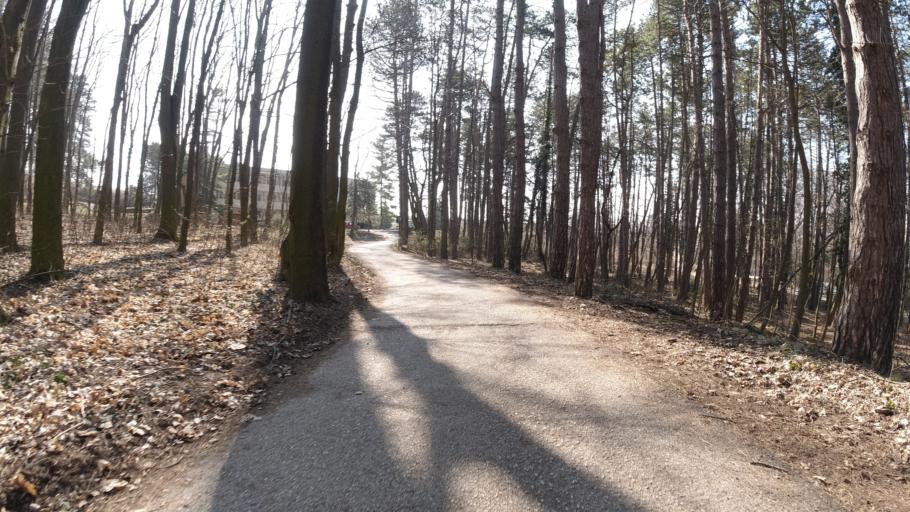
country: SK
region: Trnavsky
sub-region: Okres Trnava
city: Piestany
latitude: 48.5805
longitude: 17.8383
